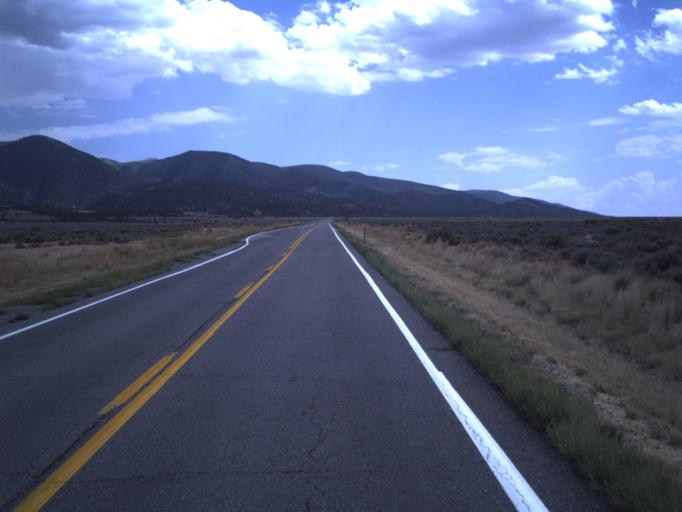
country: US
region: Utah
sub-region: Tooele County
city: Tooele
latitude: 40.3629
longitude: -112.3350
